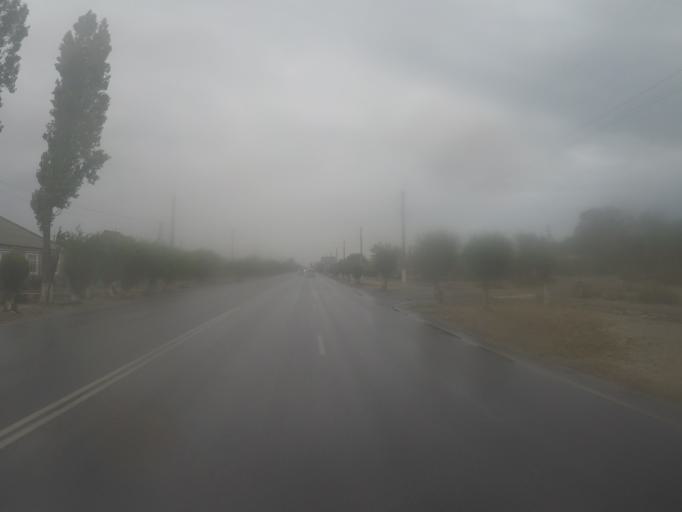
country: KG
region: Ysyk-Koel
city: Balykchy
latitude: 42.4607
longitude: 76.2088
